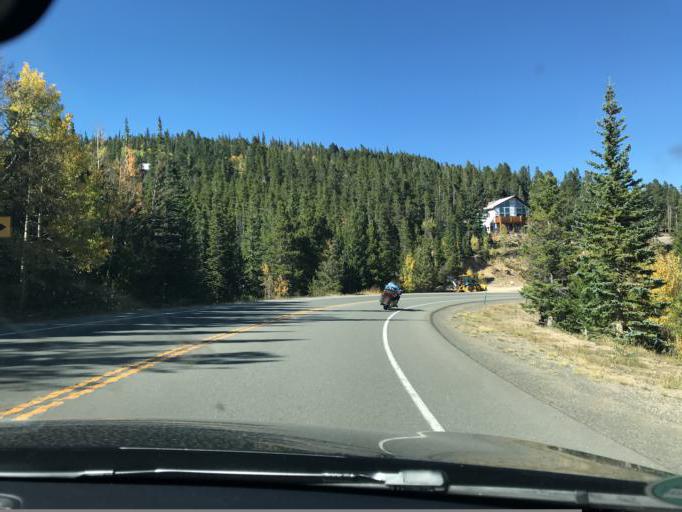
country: US
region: Colorado
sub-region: Boulder County
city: Nederland
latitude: 40.0726
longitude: -105.5121
